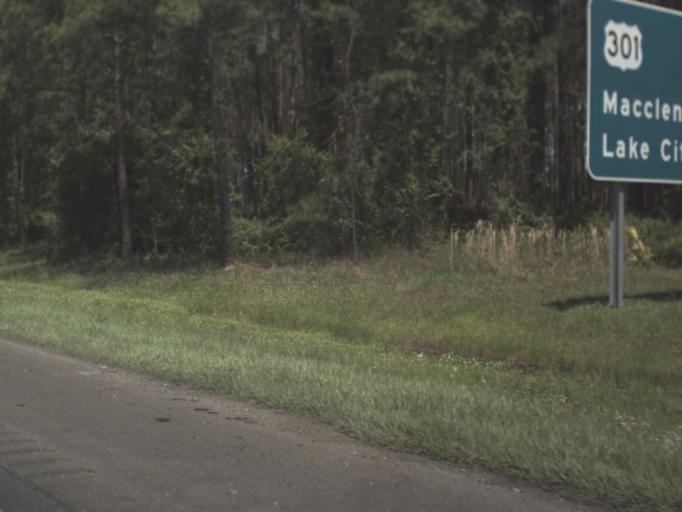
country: US
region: Florida
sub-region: Duval County
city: Baldwin
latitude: 30.3056
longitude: -81.8898
